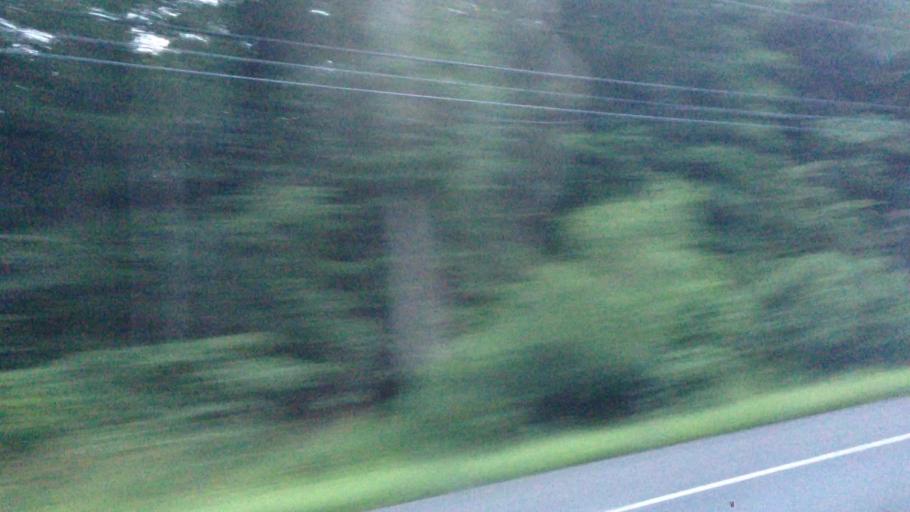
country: US
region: New York
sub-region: Dutchess County
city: Red Hook
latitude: 41.9848
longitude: -73.9103
